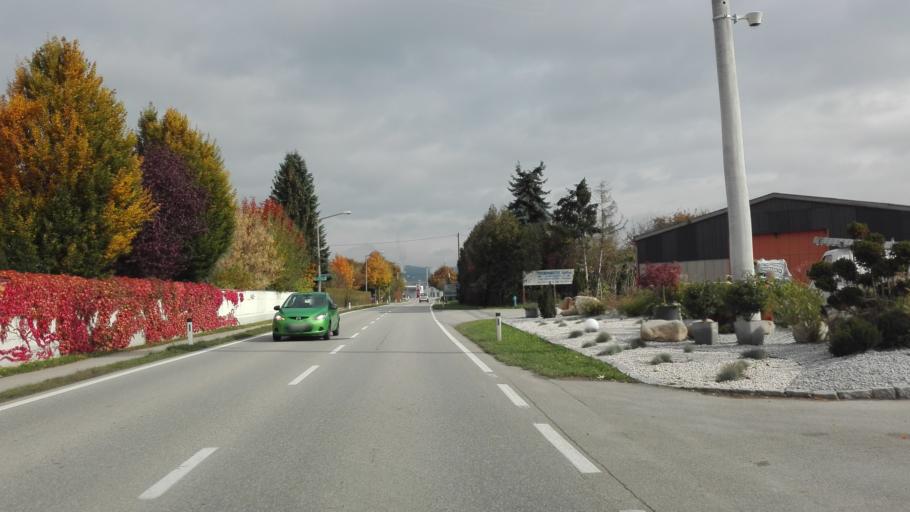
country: AT
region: Upper Austria
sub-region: Politischer Bezirk Urfahr-Umgebung
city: Feldkirchen an der Donau
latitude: 48.3596
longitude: 13.9972
